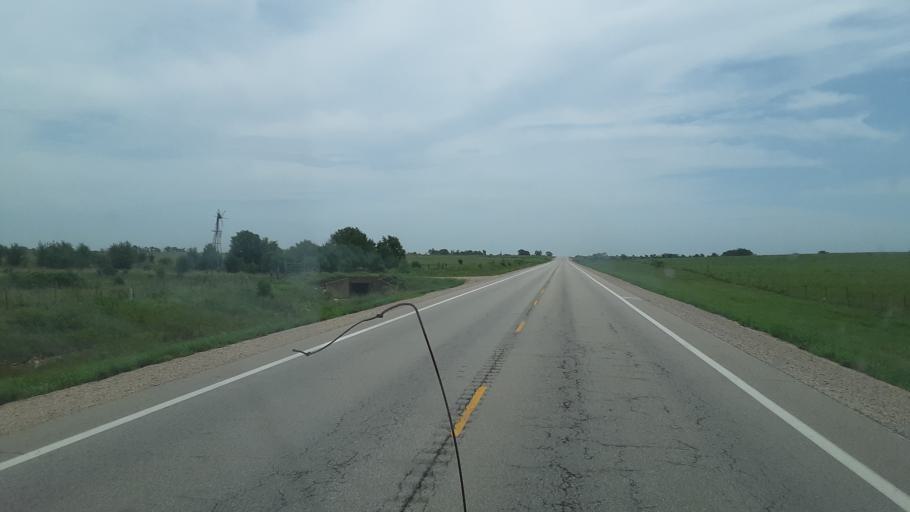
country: US
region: Kansas
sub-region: Woodson County
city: Yates Center
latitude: 37.8363
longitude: -95.9101
